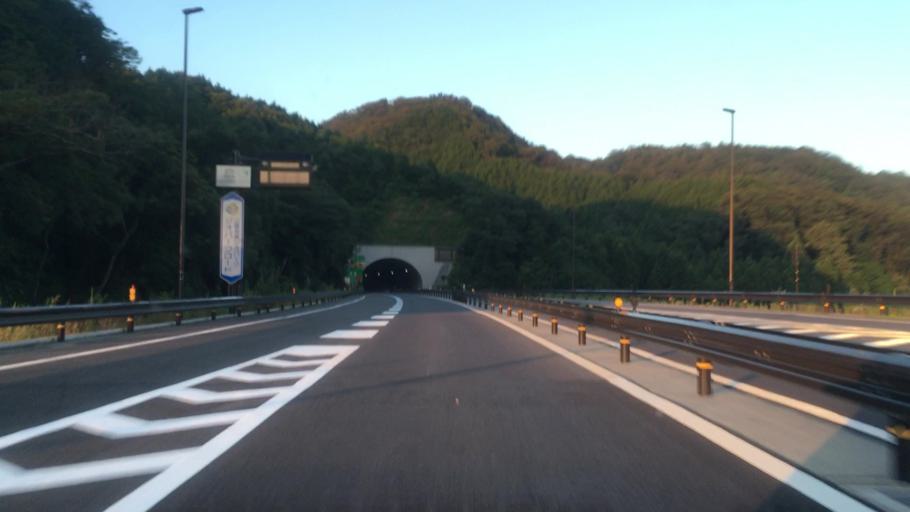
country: JP
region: Tottori
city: Tottori
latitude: 35.5731
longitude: 134.3179
